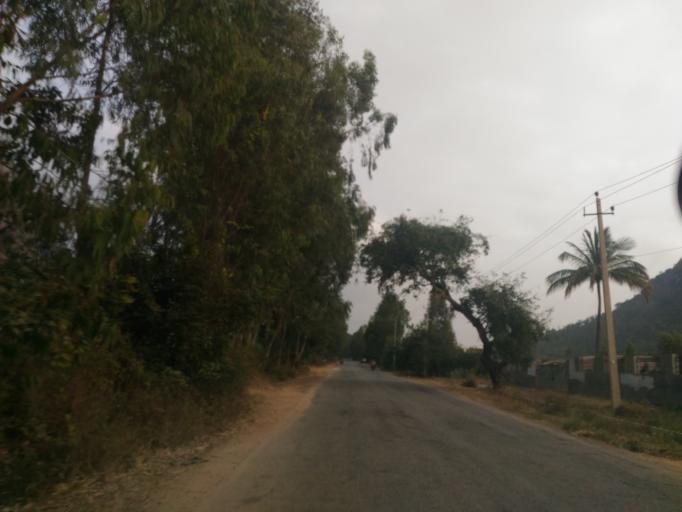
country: IN
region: Karnataka
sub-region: Chikkaballapur
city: Chik Ballapur
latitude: 13.3497
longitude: 77.6626
